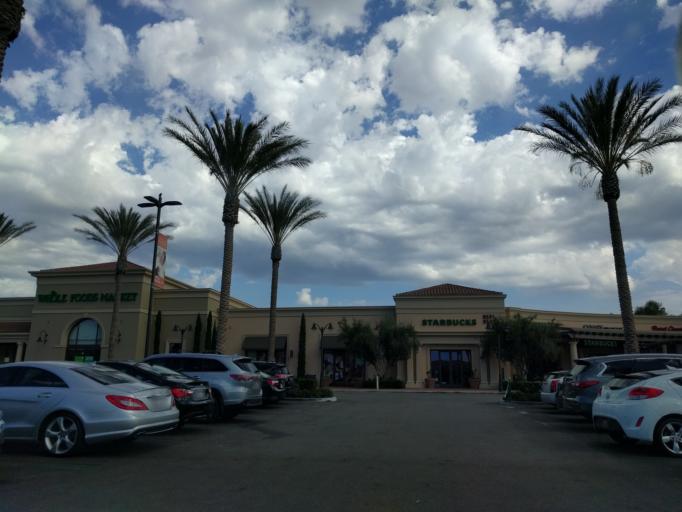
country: US
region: California
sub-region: Orange County
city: Laguna Woods
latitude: 33.6456
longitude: -117.7439
